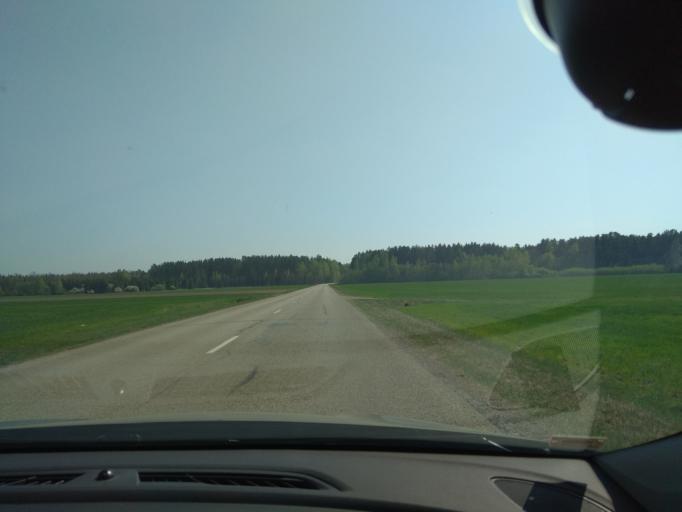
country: LT
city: Linkuva
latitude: 55.9996
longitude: 24.1663
